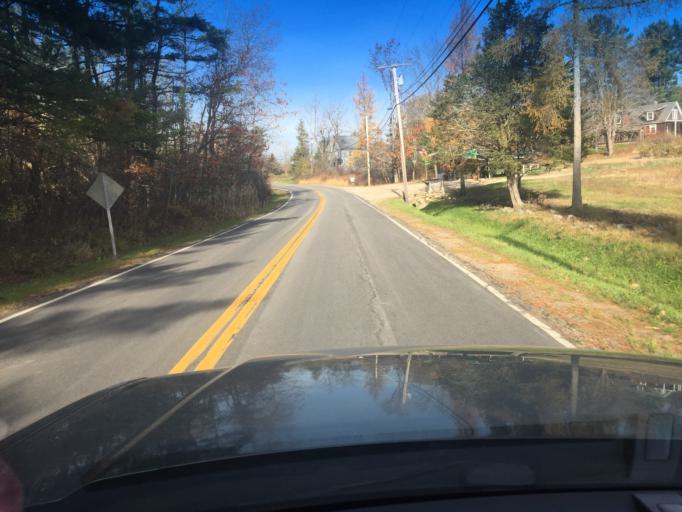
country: US
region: Maine
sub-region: York County
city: Eliot
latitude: 43.1768
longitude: -70.7252
